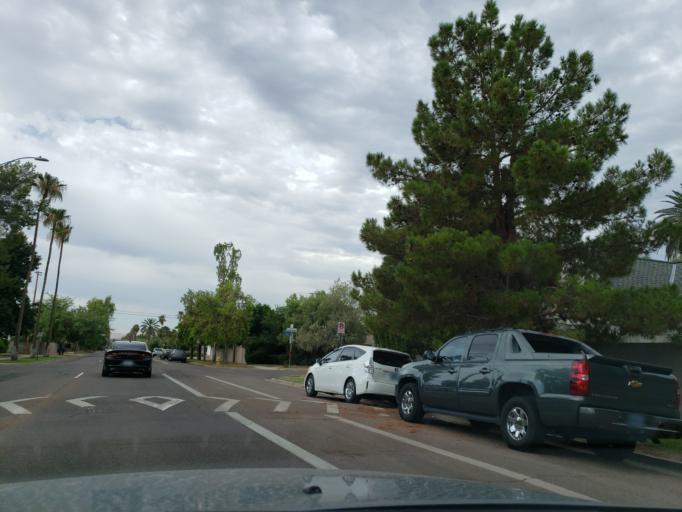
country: US
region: Arizona
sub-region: Maricopa County
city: Phoenix
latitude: 33.4689
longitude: -112.0803
